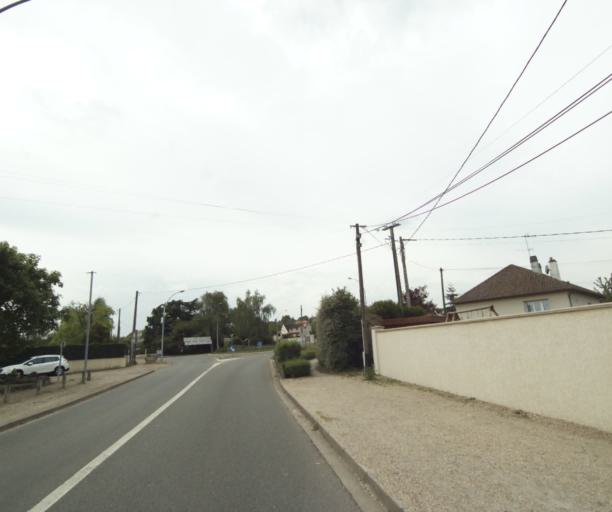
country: FR
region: Ile-de-France
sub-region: Departement des Yvelines
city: Bouafle
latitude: 48.9684
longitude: 1.9050
